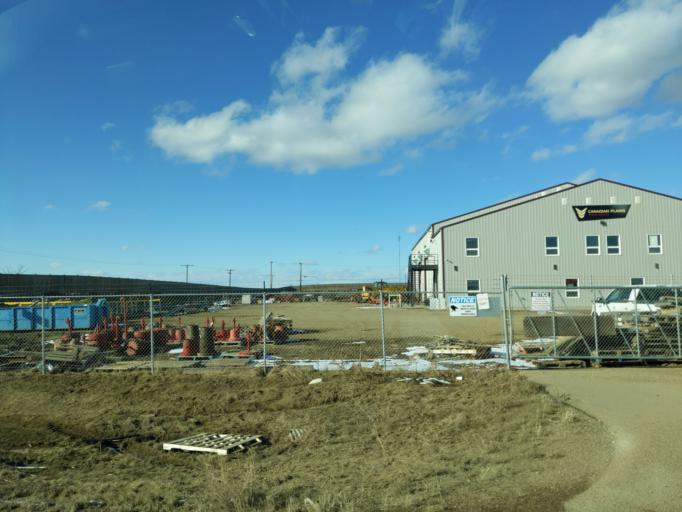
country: CA
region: Saskatchewan
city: Lloydminster
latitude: 53.2440
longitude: -109.9784
